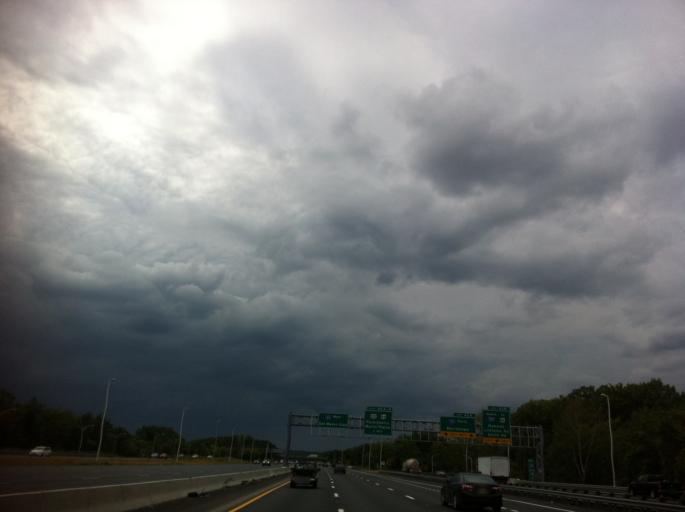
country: US
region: New Jersey
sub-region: Morris County
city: East Hanover
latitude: 40.8600
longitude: -74.3805
